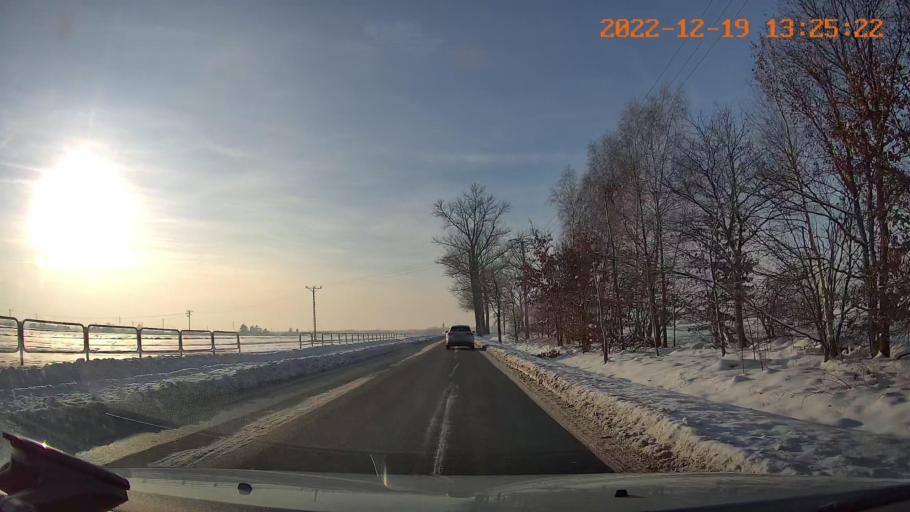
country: PL
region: Silesian Voivodeship
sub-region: Powiat bierunsko-ledzinski
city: Ledziny
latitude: 50.1052
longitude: 19.1473
